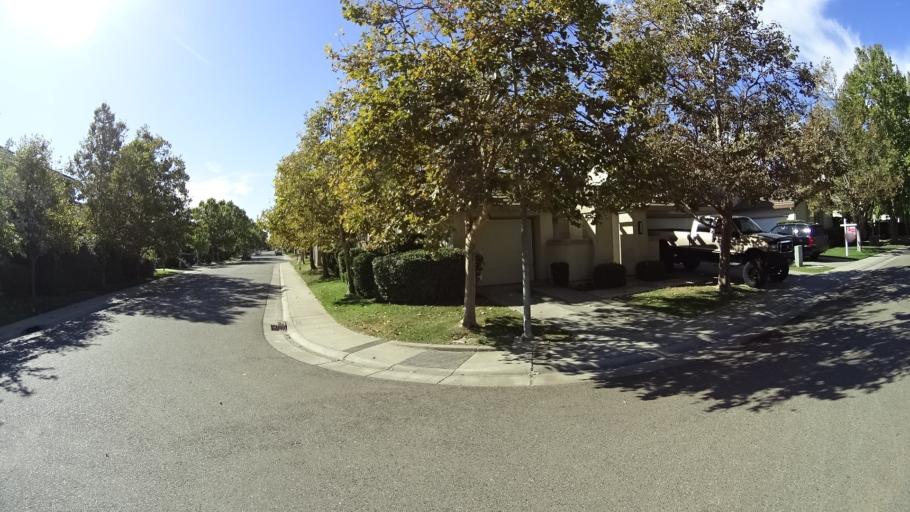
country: US
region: California
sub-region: Sacramento County
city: Laguna
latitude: 38.4199
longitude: -121.4822
